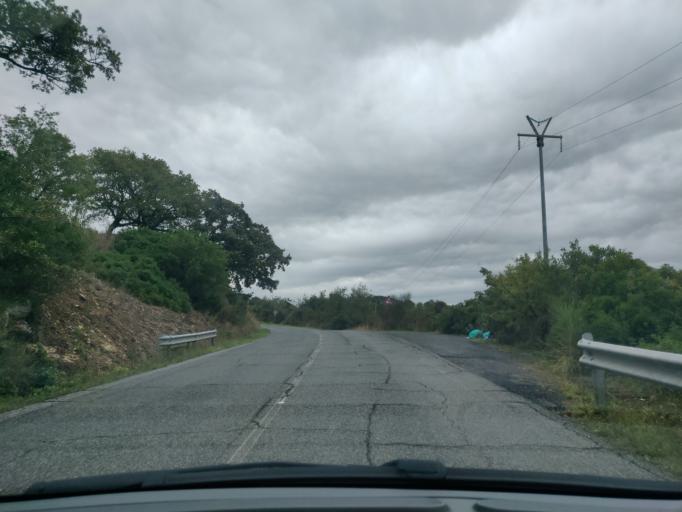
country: IT
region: Latium
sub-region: Citta metropolitana di Roma Capitale
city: Allumiere
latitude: 42.1254
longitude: 11.8616
